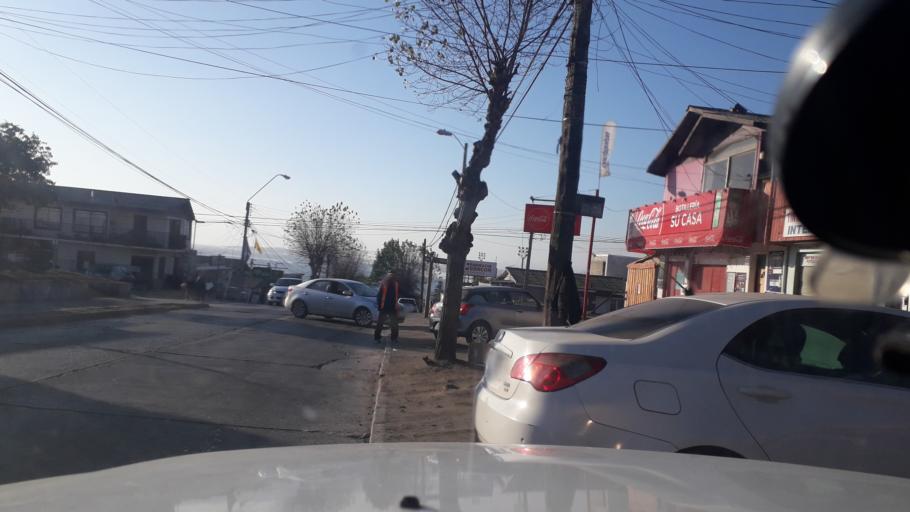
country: CL
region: Valparaiso
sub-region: Provincia de Valparaiso
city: Vina del Mar
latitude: -32.9251
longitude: -71.5166
